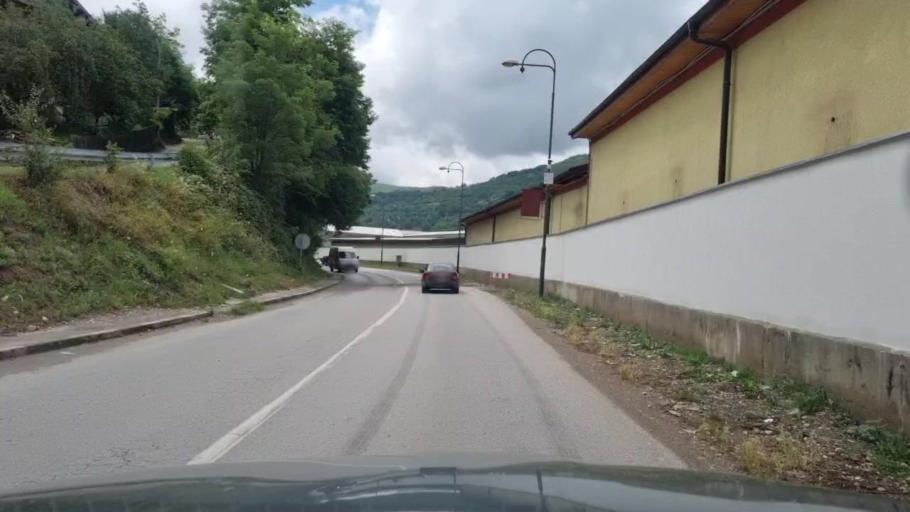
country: BA
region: Federation of Bosnia and Herzegovina
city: Gorazde
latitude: 43.6569
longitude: 18.9699
